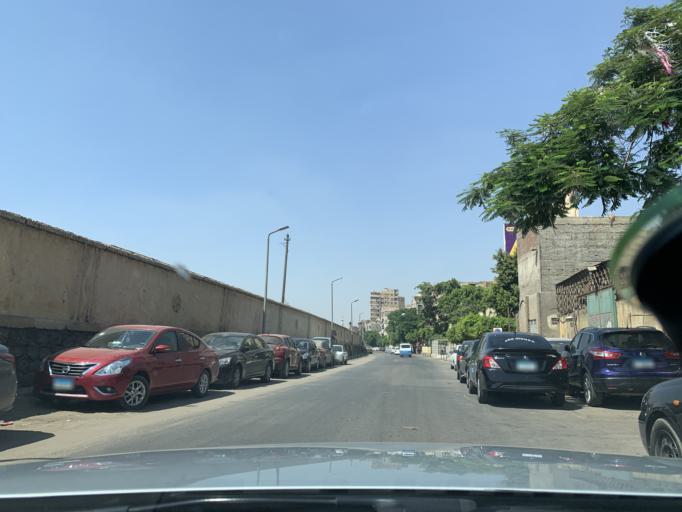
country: EG
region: Muhafazat al Qahirah
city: Cairo
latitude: 30.0674
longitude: 31.2534
